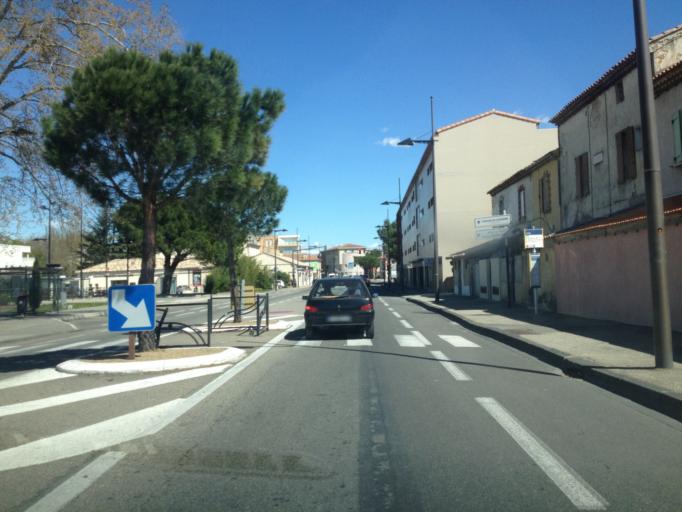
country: FR
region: Provence-Alpes-Cote d'Azur
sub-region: Departement du Vaucluse
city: Le Pontet
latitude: 43.9602
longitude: 4.8555
